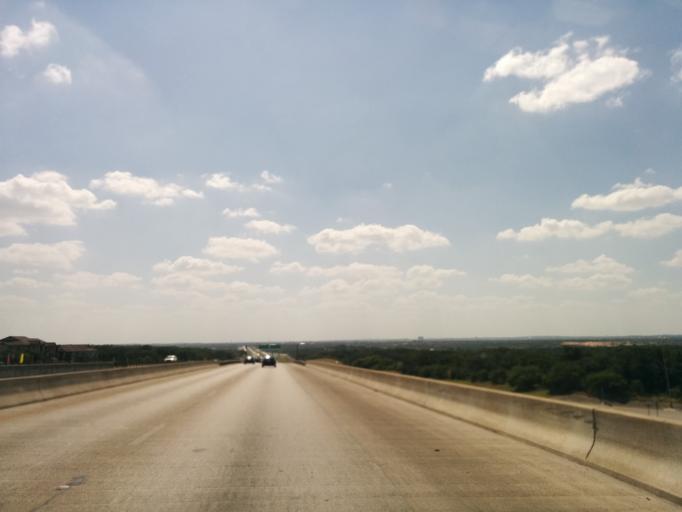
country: US
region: Texas
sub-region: Bexar County
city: Live Oak
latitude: 29.6026
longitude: -98.3872
